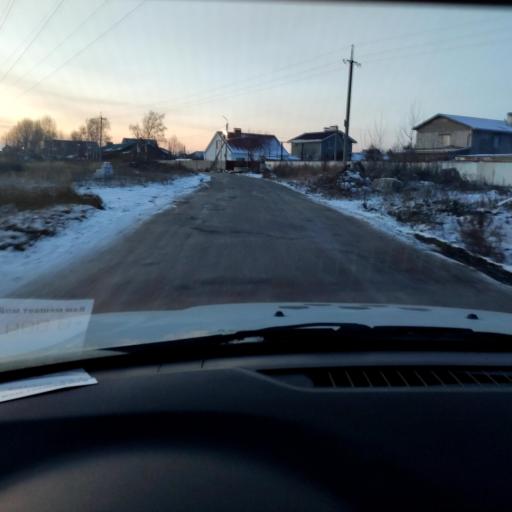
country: RU
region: Samara
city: Tol'yatti
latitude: 53.5597
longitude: 49.3877
